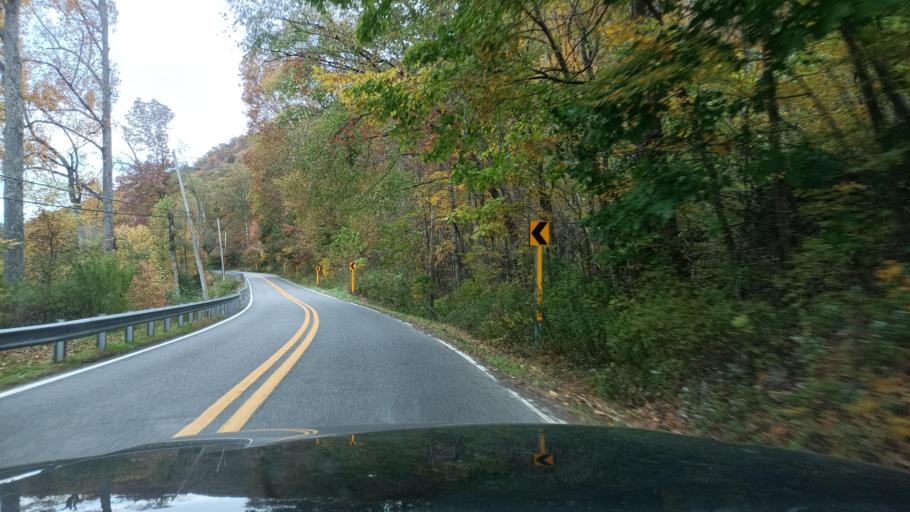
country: US
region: West Virginia
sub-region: Preston County
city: Terra Alta
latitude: 39.3066
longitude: -79.6367
